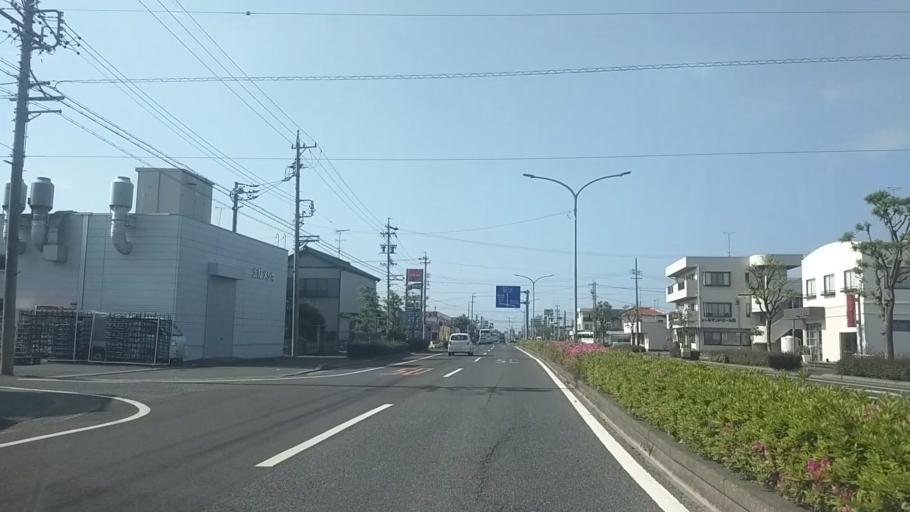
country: JP
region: Shizuoka
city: Hamamatsu
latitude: 34.7024
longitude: 137.7573
